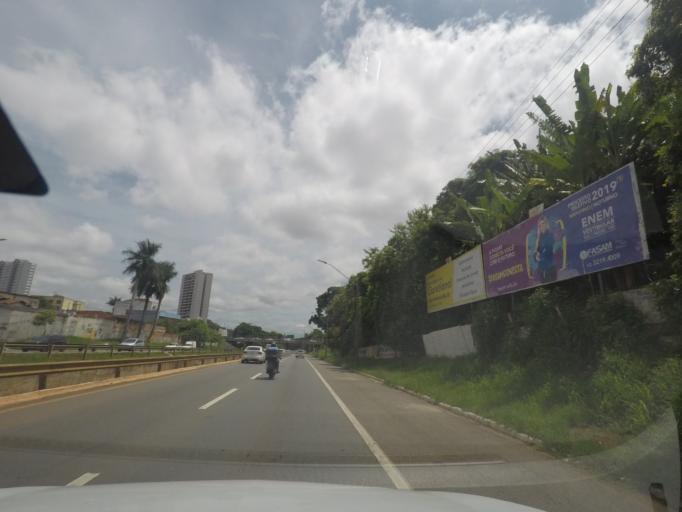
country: BR
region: Goias
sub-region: Goiania
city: Goiania
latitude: -16.6744
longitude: -49.2498
